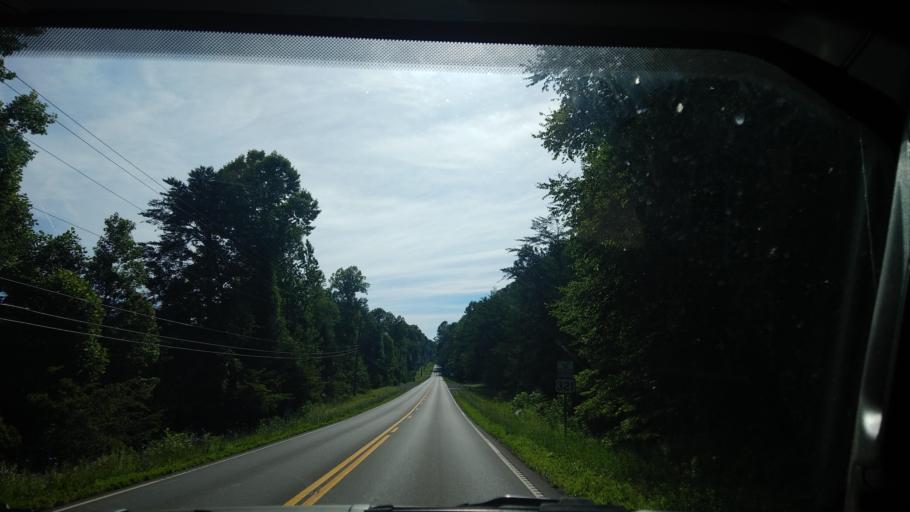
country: US
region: Tennessee
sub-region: Sevier County
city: Gatlinburg
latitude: 35.7600
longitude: -83.3418
